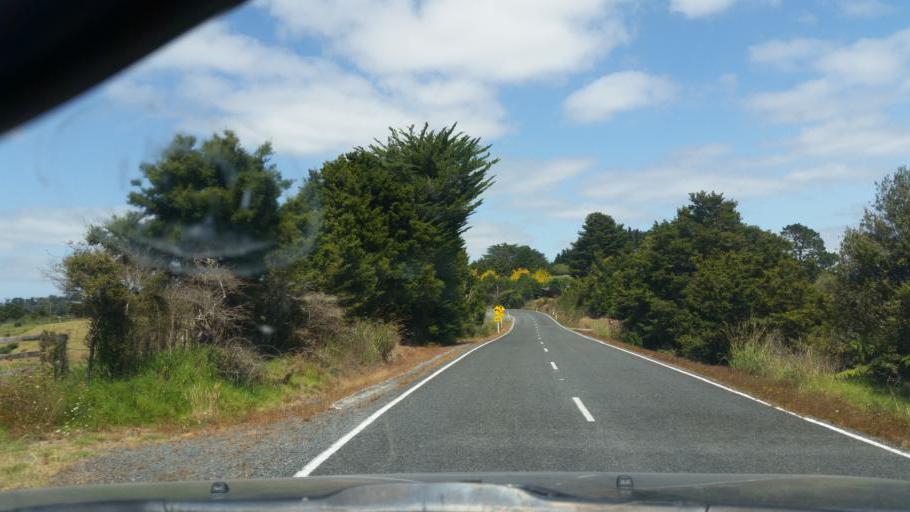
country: NZ
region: Northland
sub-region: Whangarei
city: Ruakaka
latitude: -36.0547
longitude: 174.2740
